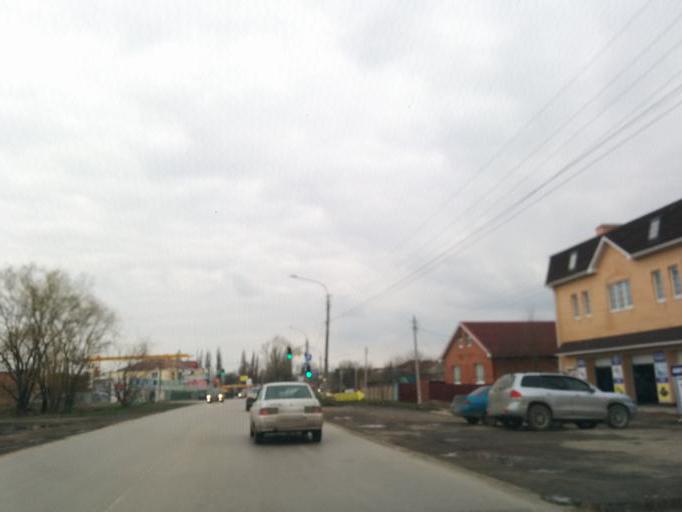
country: RU
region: Rostov
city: Novocherkassk
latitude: 47.4556
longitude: 40.1024
